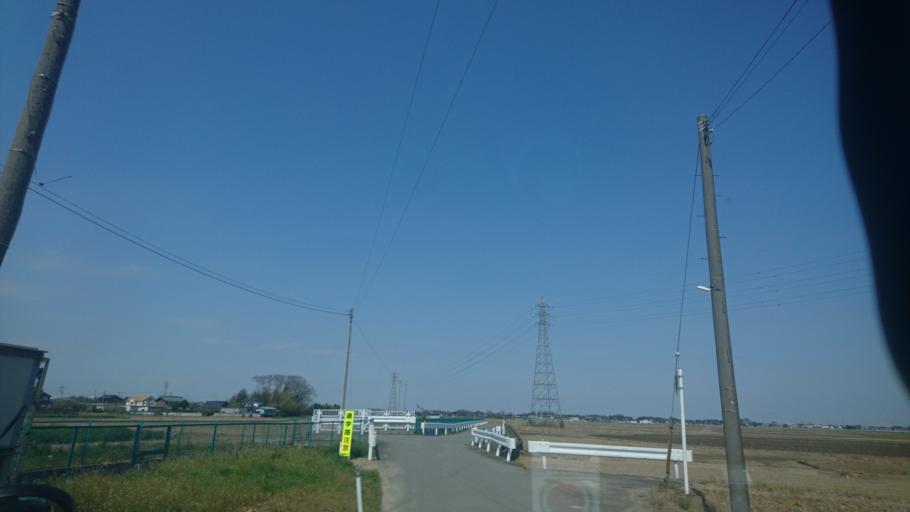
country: JP
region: Ibaraki
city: Ishige
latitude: 36.0845
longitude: 139.9766
